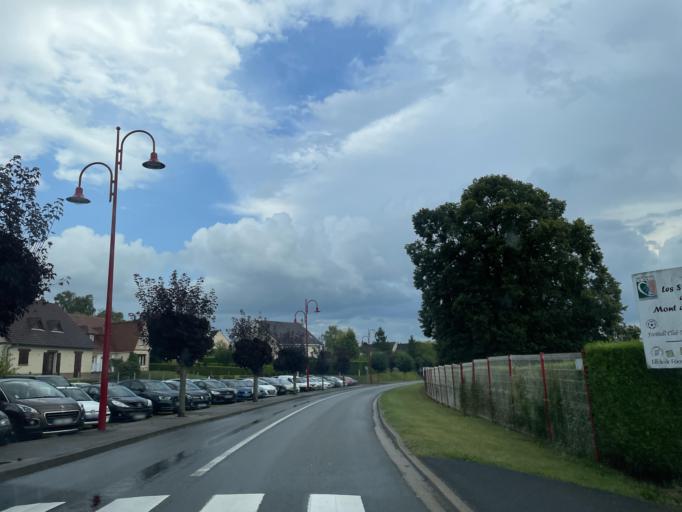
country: FR
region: Haute-Normandie
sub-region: Departement de la Seine-Maritime
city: Neufchatel-en-Bray
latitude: 49.7425
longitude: 1.4366
